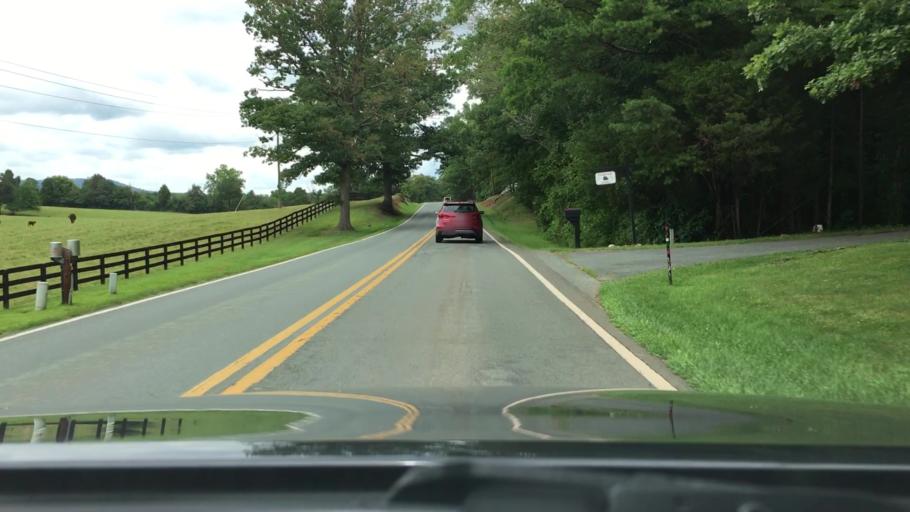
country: US
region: Virginia
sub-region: Fluvanna County
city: Lake Monticello
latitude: 38.0459
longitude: -78.3285
